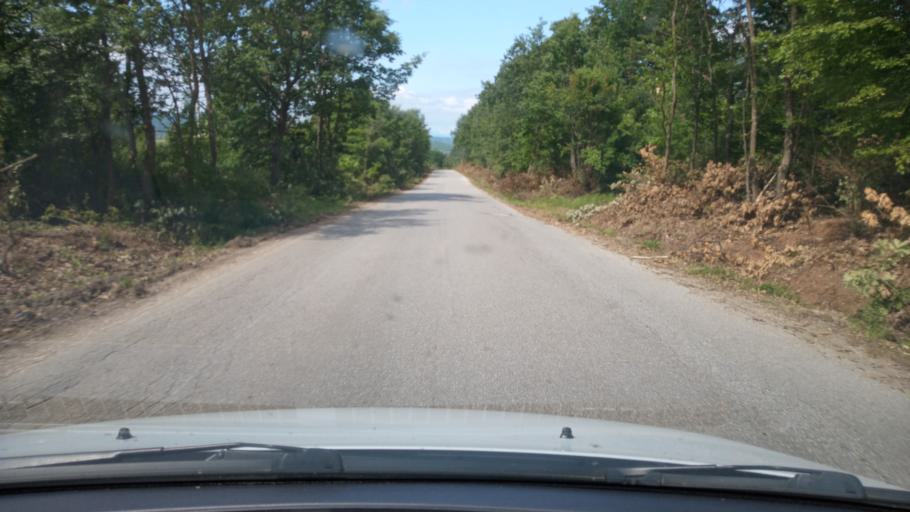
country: BG
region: Lovech
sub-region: Obshtina Lukovit
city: Lukovit
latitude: 43.1897
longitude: 24.0941
